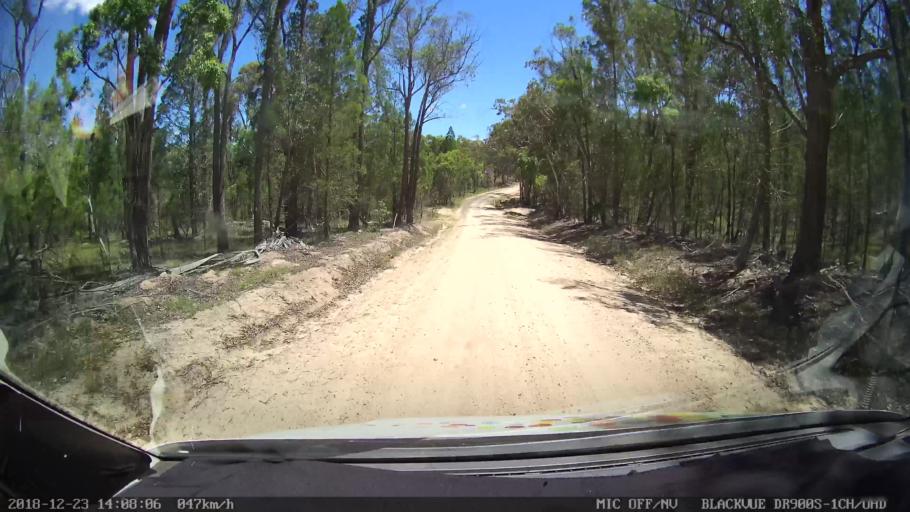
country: AU
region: New South Wales
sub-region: Tamworth Municipality
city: Manilla
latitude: -30.6402
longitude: 151.0698
